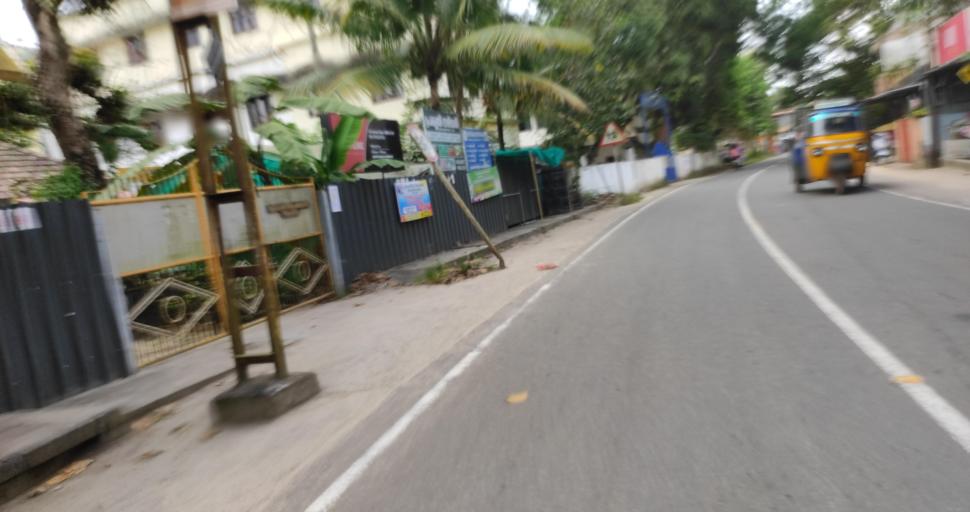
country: IN
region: Kerala
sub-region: Alappuzha
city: Shertallai
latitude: 9.6553
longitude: 76.3179
